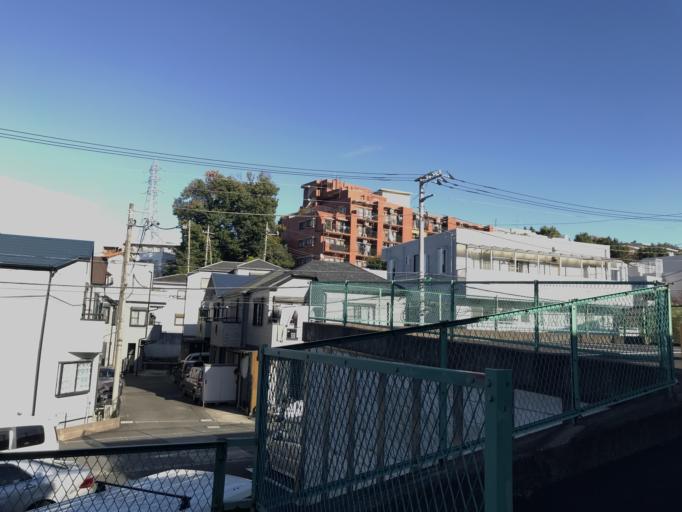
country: JP
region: Kanagawa
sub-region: Kawasaki-shi
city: Kawasaki
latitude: 35.5645
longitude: 139.6154
